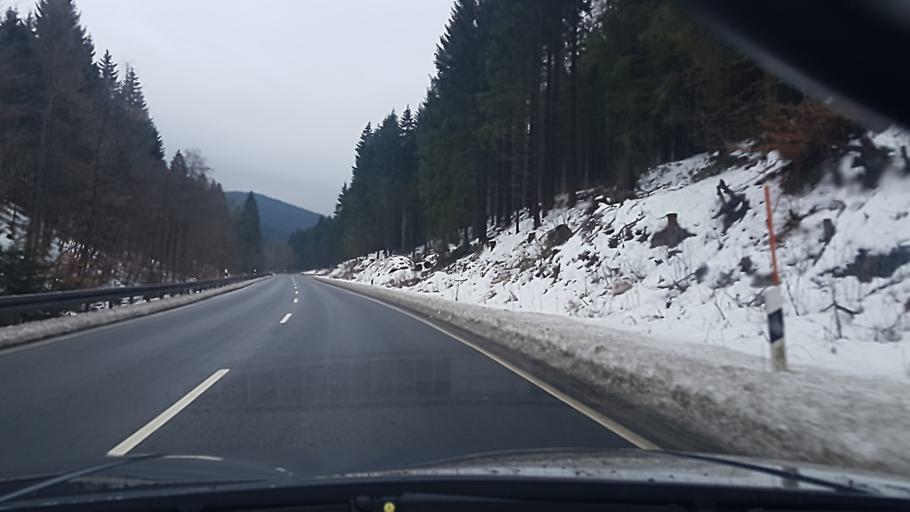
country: DE
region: Lower Saxony
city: Goslar
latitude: 51.8752
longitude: 10.3921
